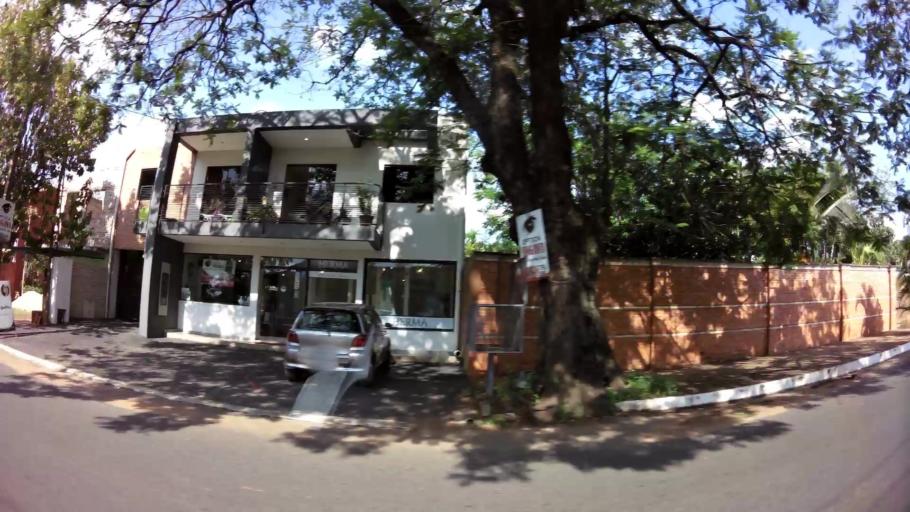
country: PY
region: Central
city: Fernando de la Mora
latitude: -25.3241
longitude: -57.5301
